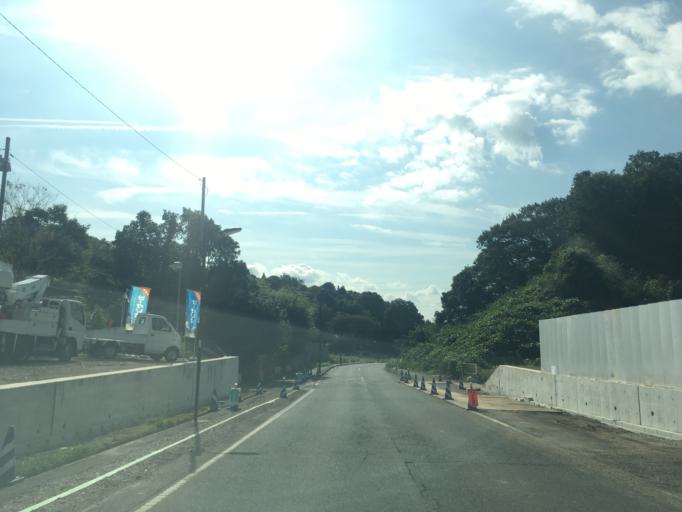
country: JP
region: Tokyo
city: Hino
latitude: 35.6068
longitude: 139.4082
